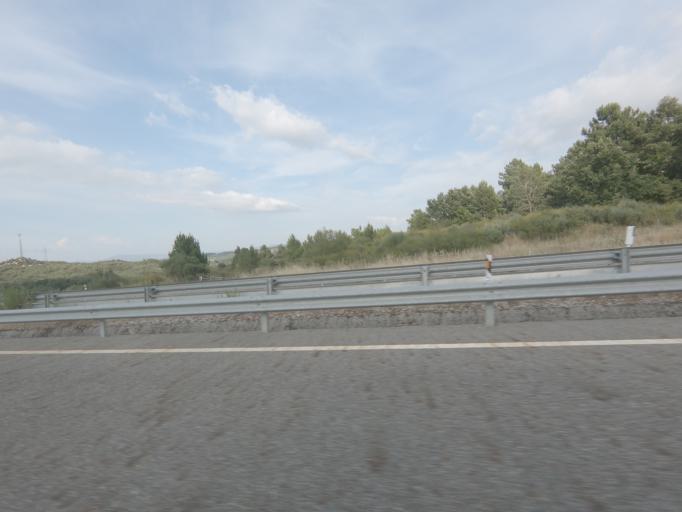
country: PT
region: Vila Real
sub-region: Chaves
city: Chaves
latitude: 41.7219
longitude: -7.5429
